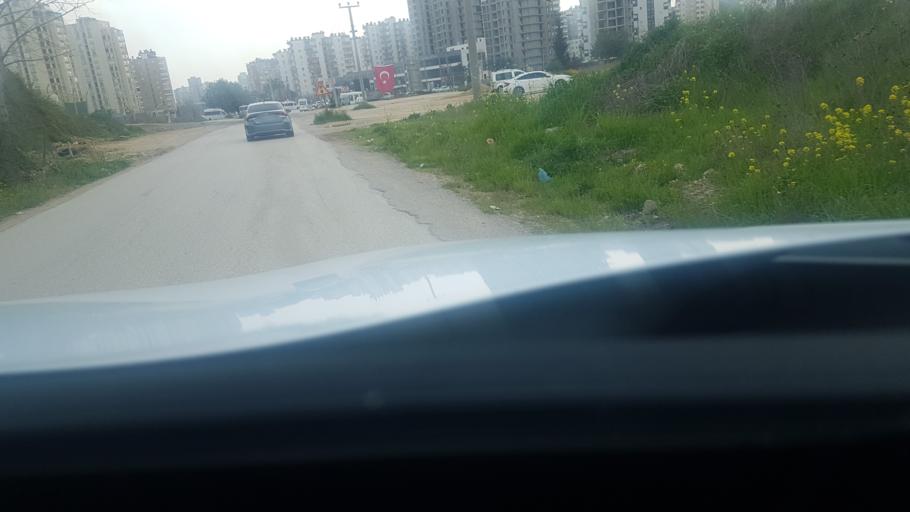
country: TR
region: Adana
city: Seyhan
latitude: 37.0547
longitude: 35.2533
